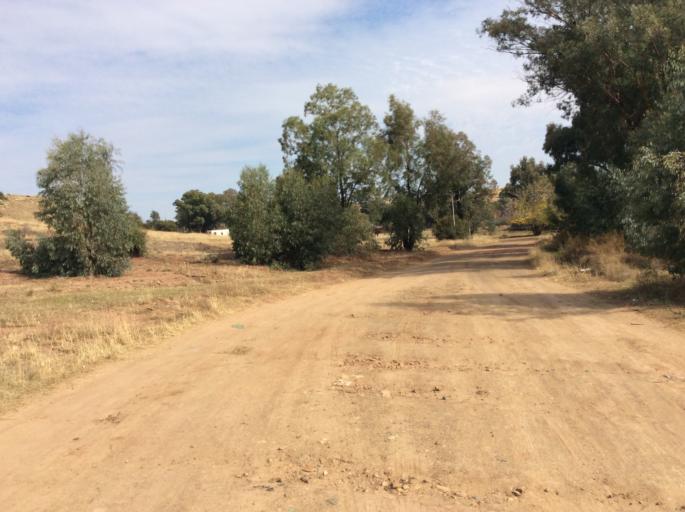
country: ZA
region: Orange Free State
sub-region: Xhariep District Municipality
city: Dewetsdorp
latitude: -29.5869
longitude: 26.6671
